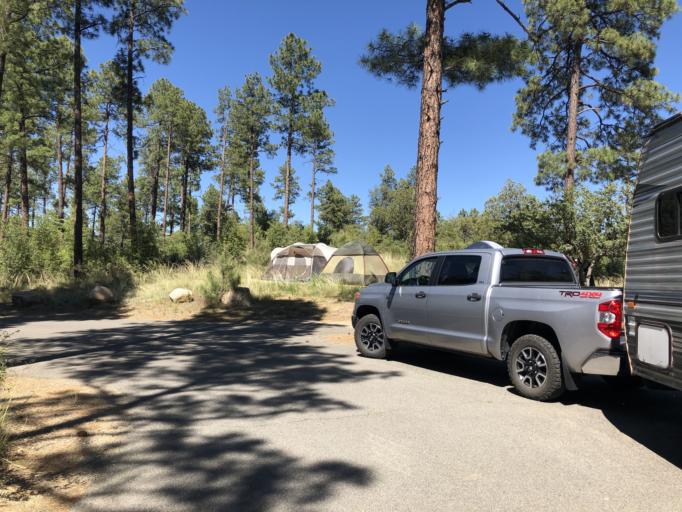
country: US
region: Arizona
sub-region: Yavapai County
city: Prescott
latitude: 34.5143
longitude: -112.3880
